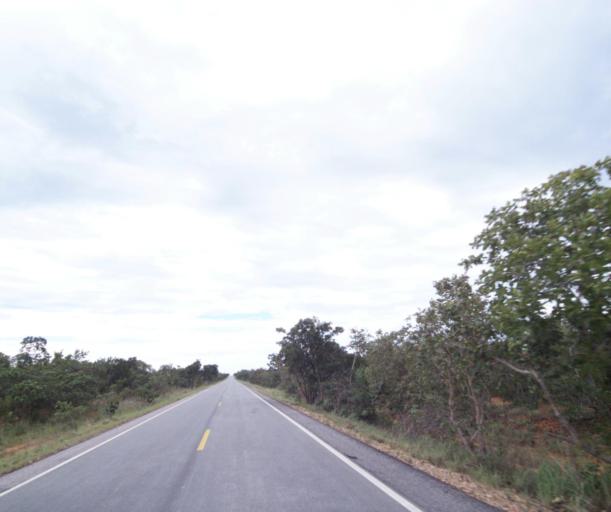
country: BR
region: Bahia
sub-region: Sao Felix Do Coribe
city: Santa Maria da Vitoria
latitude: -13.9586
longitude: -44.4458
